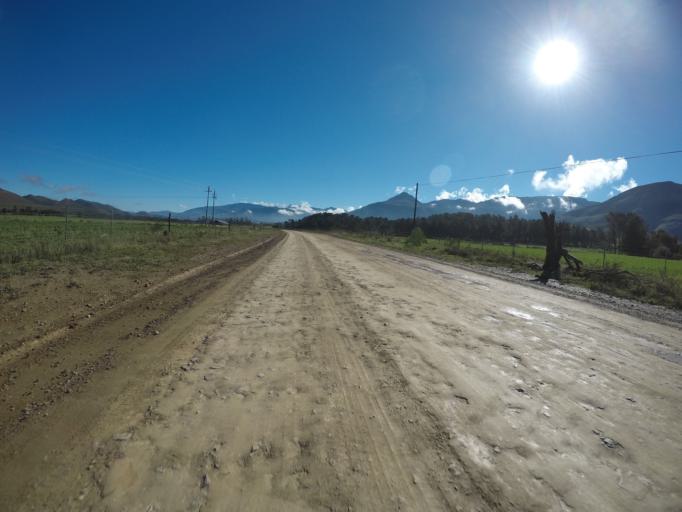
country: ZA
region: Western Cape
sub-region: Overberg District Municipality
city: Caledon
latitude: -34.0730
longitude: 19.6388
